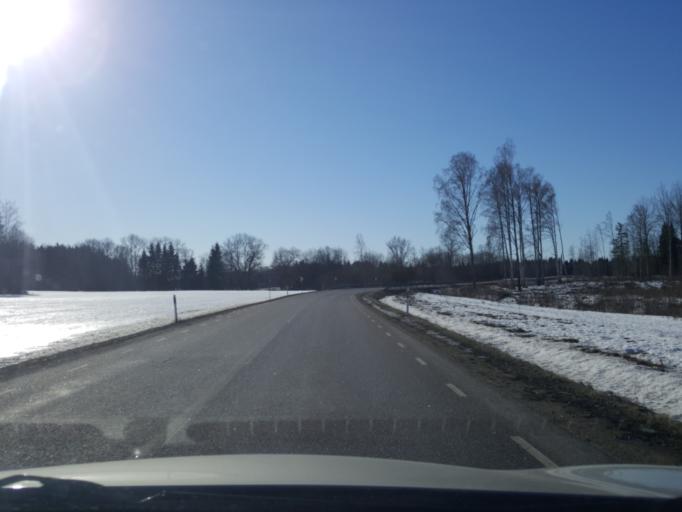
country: EE
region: Viljandimaa
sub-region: Viiratsi vald
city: Viiratsi
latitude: 58.4233
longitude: 25.6819
